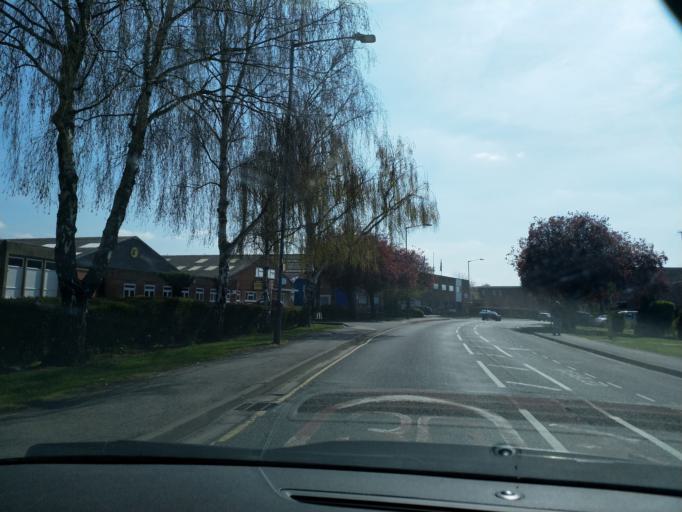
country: GB
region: England
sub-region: Warwickshire
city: Stratford-upon-Avon
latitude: 52.1964
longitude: -1.7207
